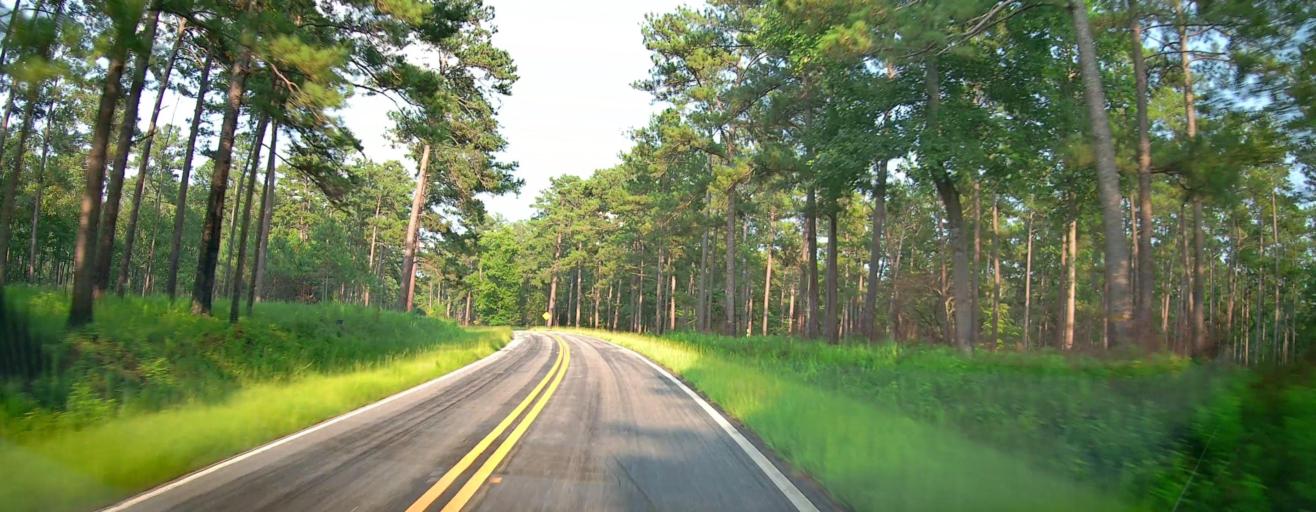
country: US
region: Georgia
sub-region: Jones County
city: Gray
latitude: 33.0989
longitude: -83.7207
